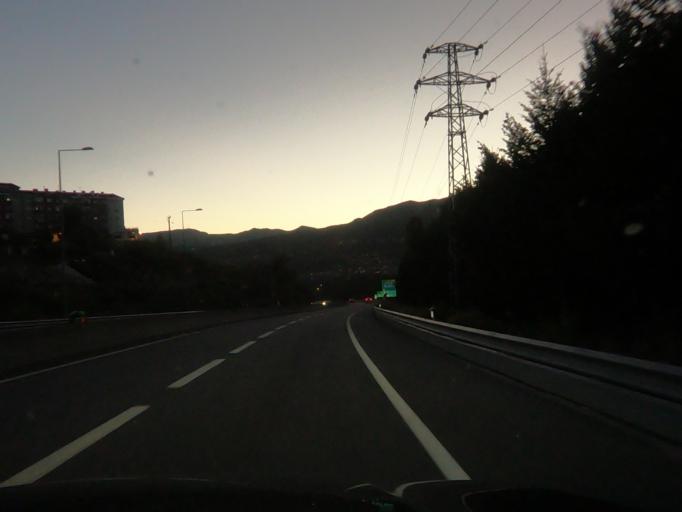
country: PT
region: Vila Real
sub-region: Vila Real
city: Vila Real
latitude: 41.3128
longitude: -7.7432
